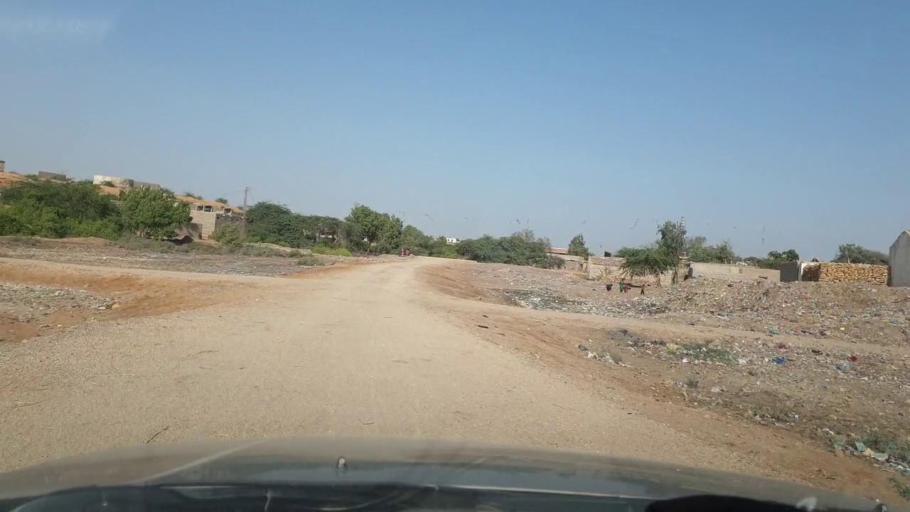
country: PK
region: Sindh
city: Daro Mehar
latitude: 25.0018
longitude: 68.1139
